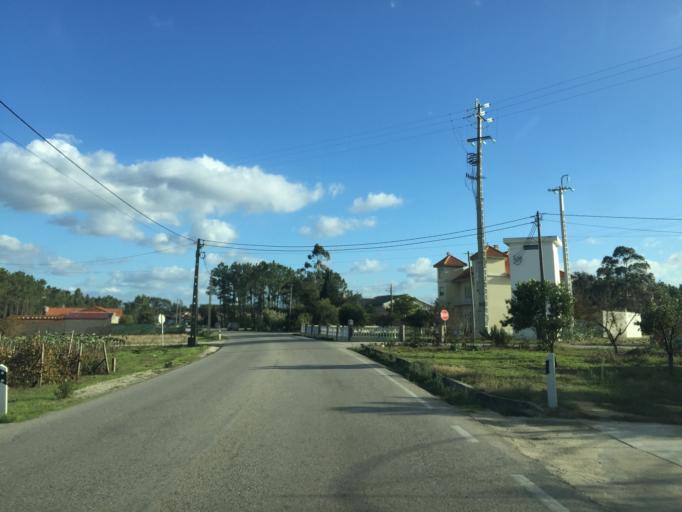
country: PT
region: Leiria
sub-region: Pombal
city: Lourical
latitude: 39.9745
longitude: -8.7972
